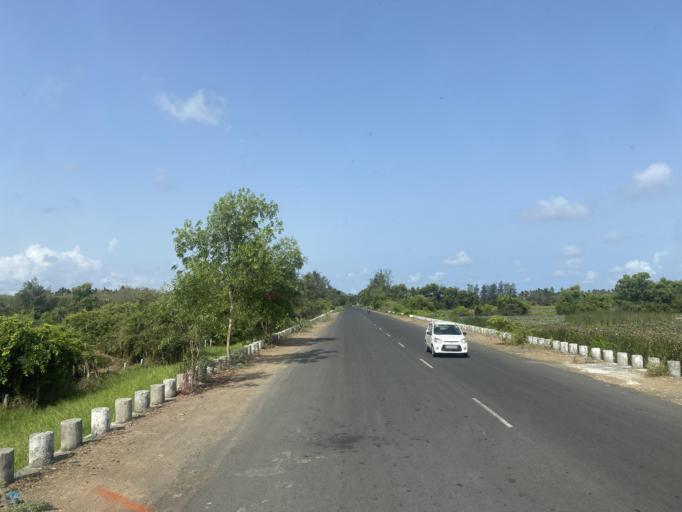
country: IN
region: Daman and Diu
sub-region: Daman District
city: Daman
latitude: 20.3504
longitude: 72.8169
